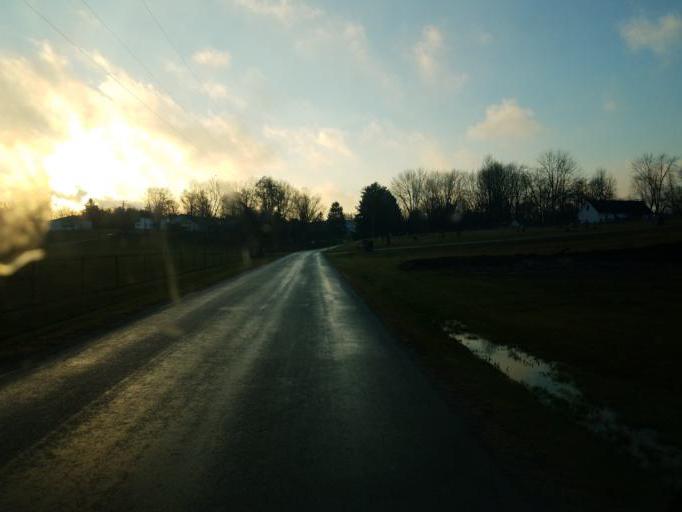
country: US
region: Ohio
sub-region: Knox County
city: Centerburg
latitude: 40.2392
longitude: -82.6821
